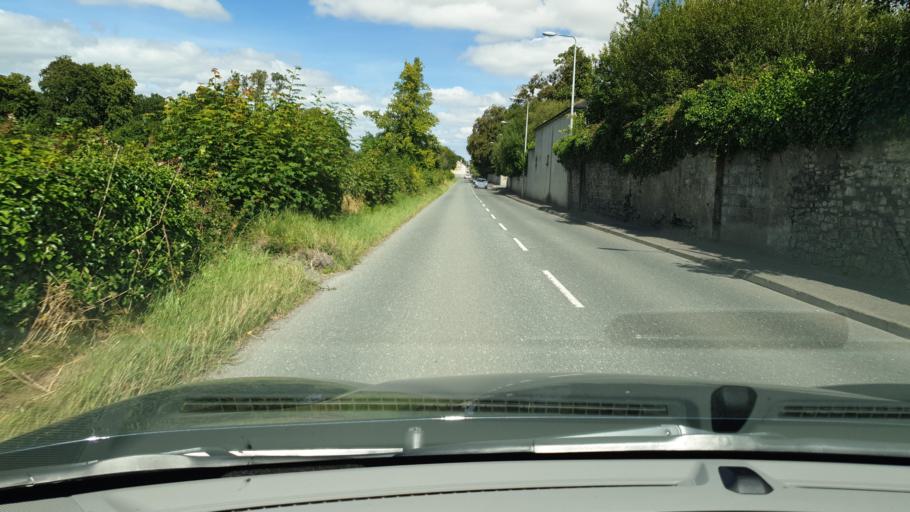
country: IE
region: Leinster
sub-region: An Mhi
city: Dunboyne
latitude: 53.4166
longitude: -6.4808
